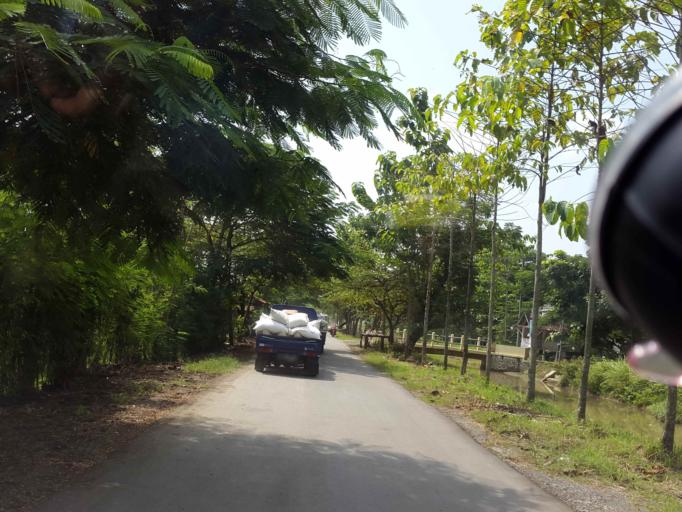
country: ID
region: Central Java
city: Pemalang
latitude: -6.9483
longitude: 109.3516
